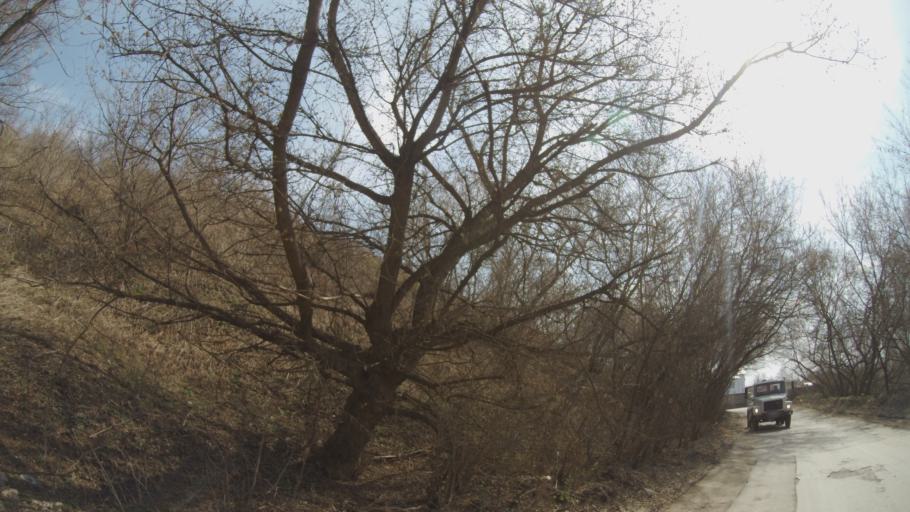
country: RU
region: Nizjnij Novgorod
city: Vyyezdnoye
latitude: 55.3868
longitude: 43.8105
